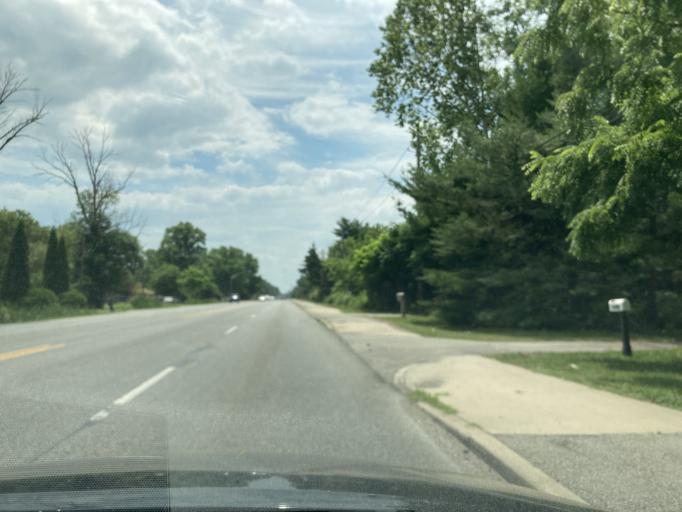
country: US
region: Indiana
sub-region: Marion County
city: Meridian Hills
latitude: 39.8741
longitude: -86.2047
